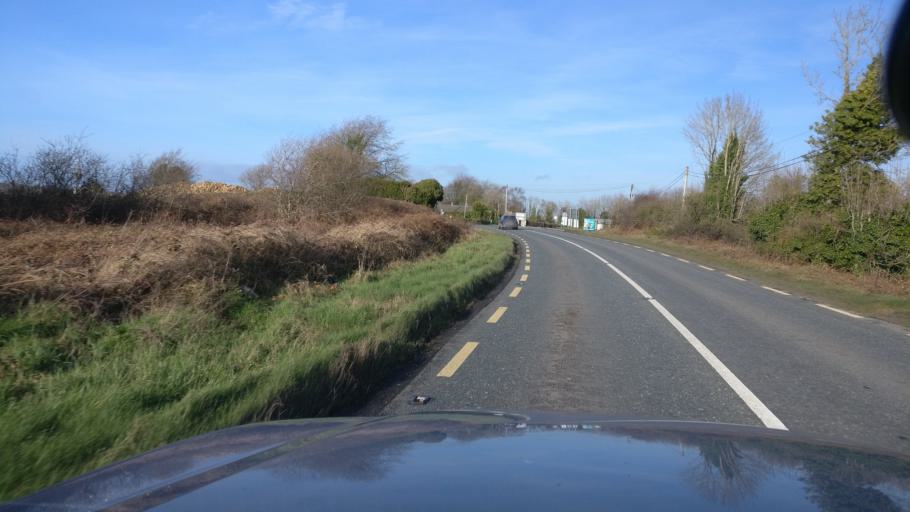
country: IE
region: Leinster
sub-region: Laois
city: Mountmellick
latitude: 53.1583
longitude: -7.3677
